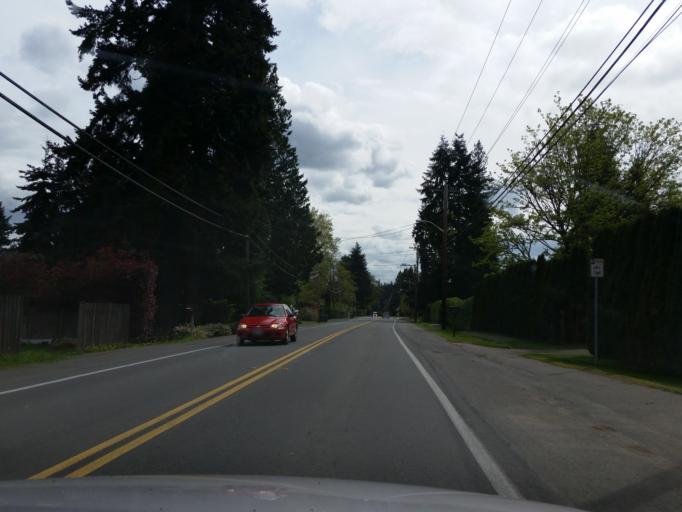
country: US
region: Washington
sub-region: King County
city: Kingsgate
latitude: 47.6952
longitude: -122.1647
